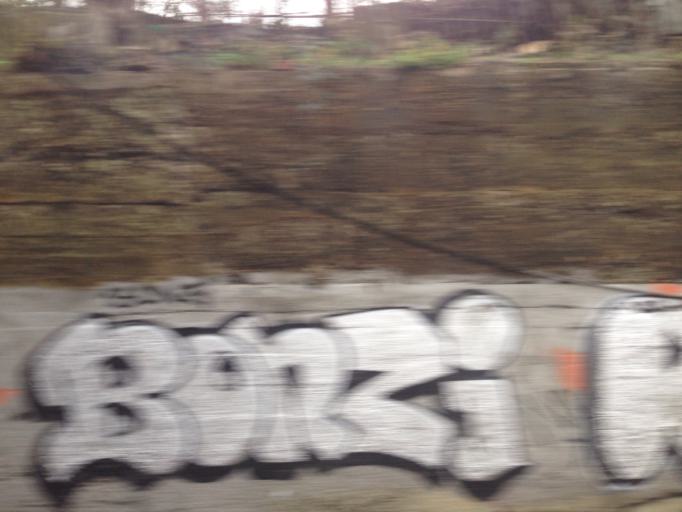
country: GB
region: England
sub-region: Greater London
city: Earlsfield
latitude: 51.4593
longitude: -0.1727
